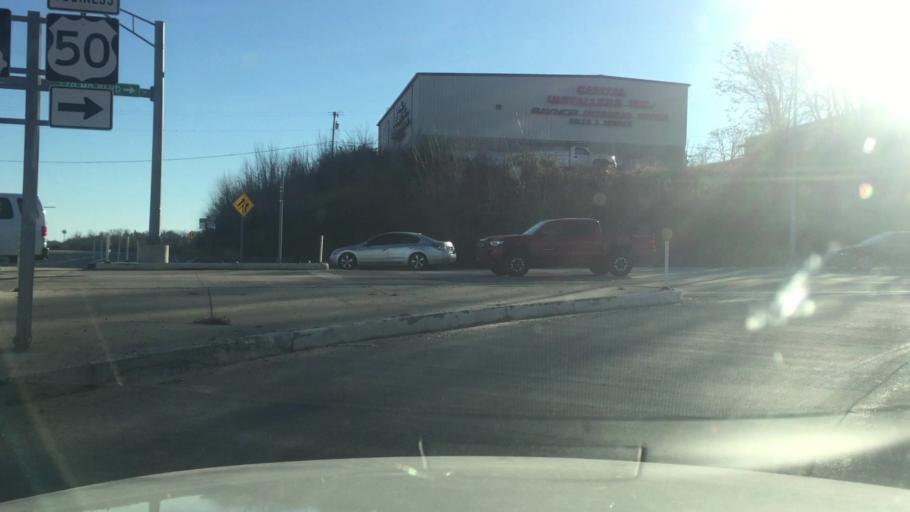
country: US
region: Missouri
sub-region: Cole County
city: Jefferson City
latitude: 38.5804
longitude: -92.2314
